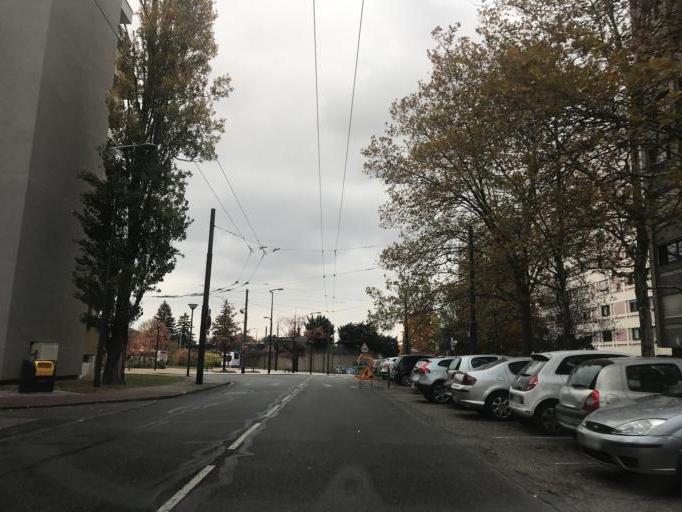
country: FR
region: Rhone-Alpes
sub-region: Departement du Rhone
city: Caluire-et-Cuire
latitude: 45.7934
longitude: 4.8490
